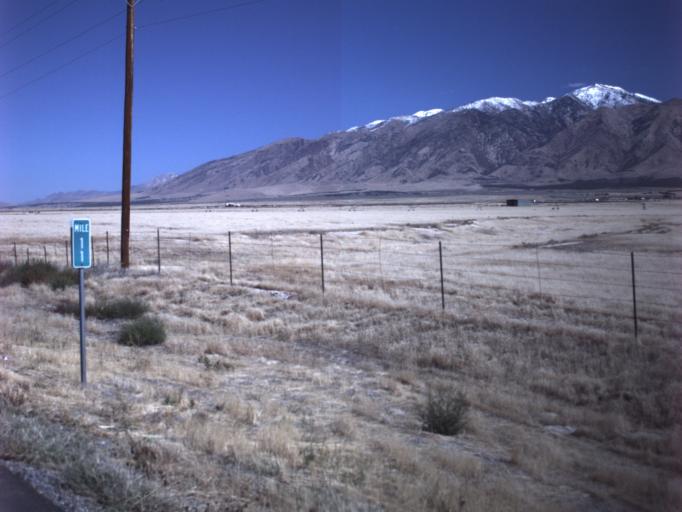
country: US
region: Utah
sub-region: Tooele County
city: Grantsville
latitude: 40.3853
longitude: -112.7471
